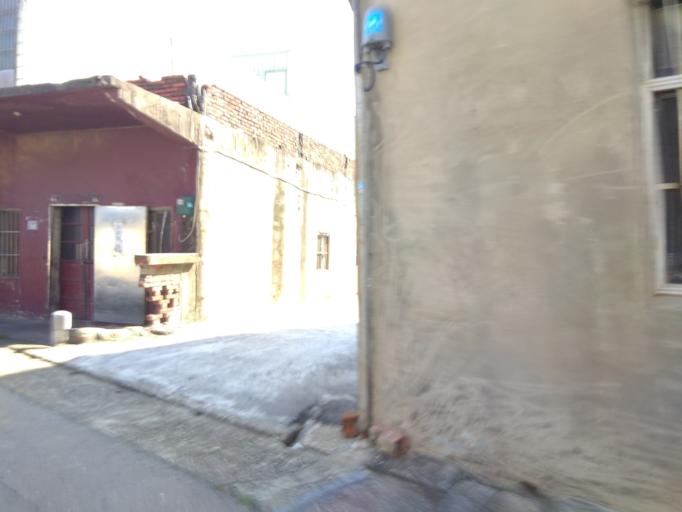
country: TW
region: Taiwan
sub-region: Hsinchu
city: Zhubei
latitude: 24.9490
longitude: 121.0095
